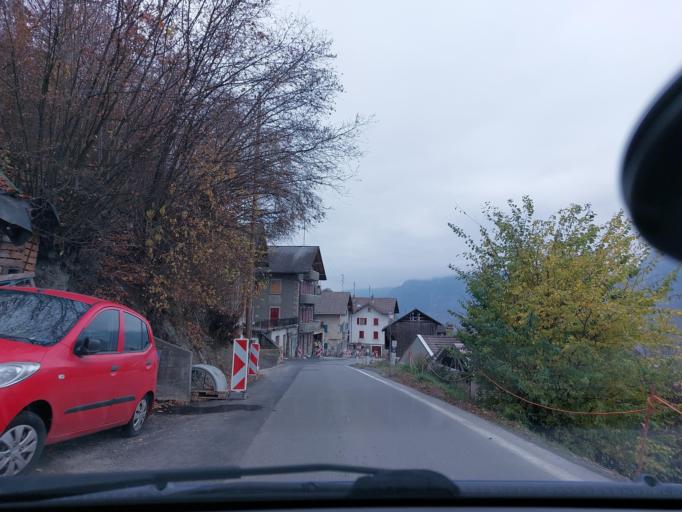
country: CH
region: Valais
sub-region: Conthey District
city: Ardon
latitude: 46.1868
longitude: 7.2709
